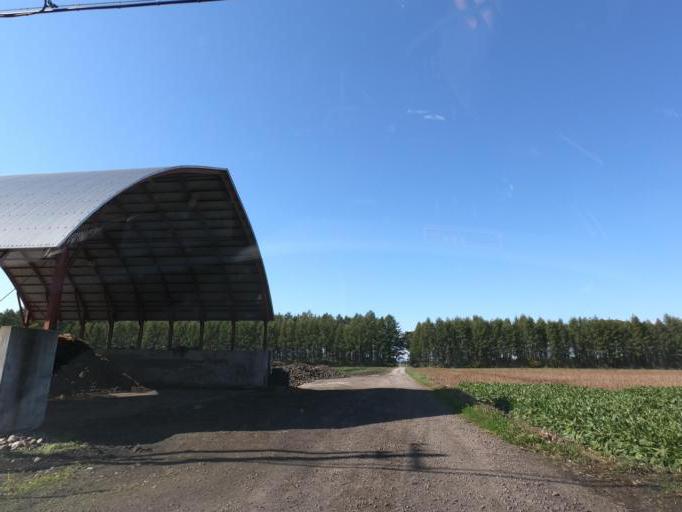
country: JP
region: Hokkaido
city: Otofuke
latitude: 43.0709
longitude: 143.2656
